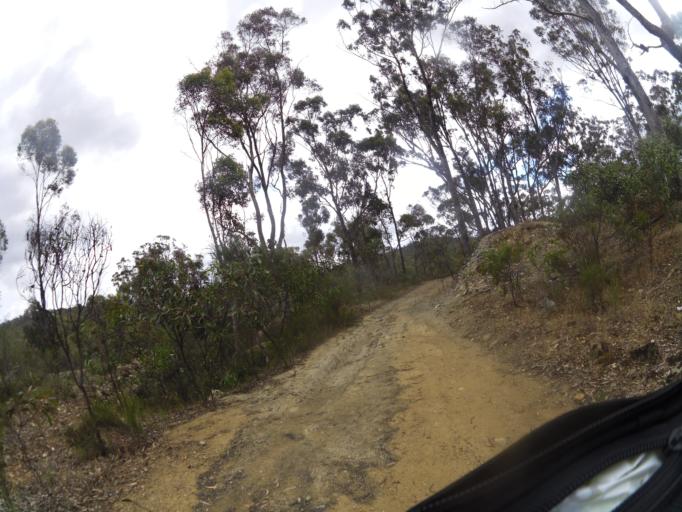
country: AU
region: Victoria
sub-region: Mount Alexander
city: Castlemaine
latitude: -37.0734
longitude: 144.2546
